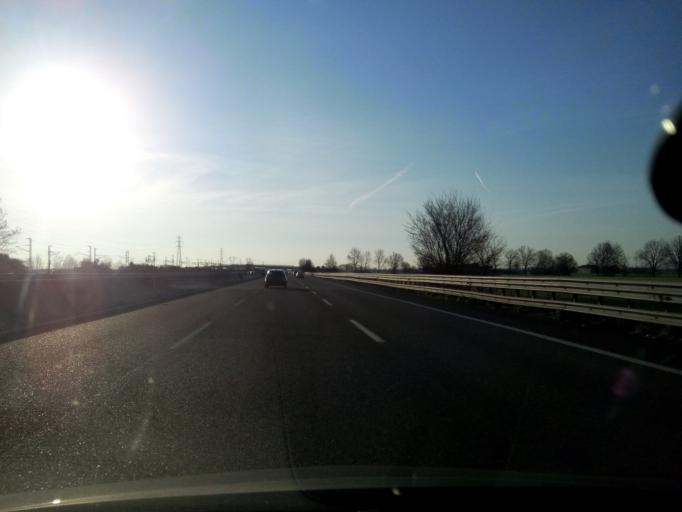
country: IT
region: Emilia-Romagna
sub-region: Provincia di Piacenza
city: Roveleto
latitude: 44.9936
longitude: 9.8314
